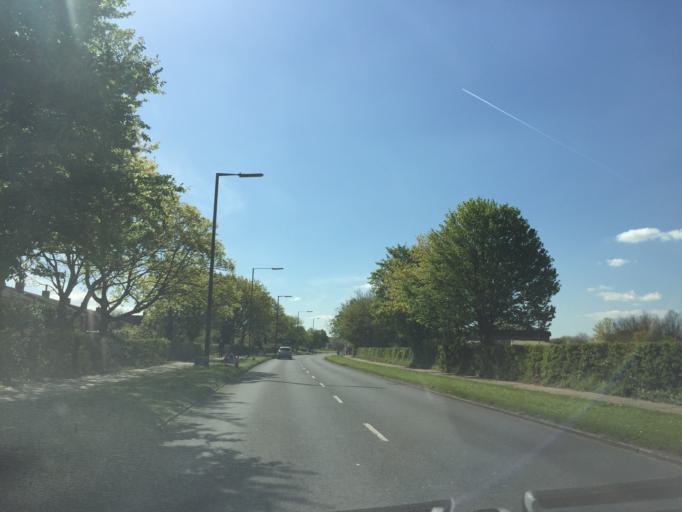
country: GB
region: England
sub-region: Essex
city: Harlow
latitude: 51.7569
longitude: 0.0900
